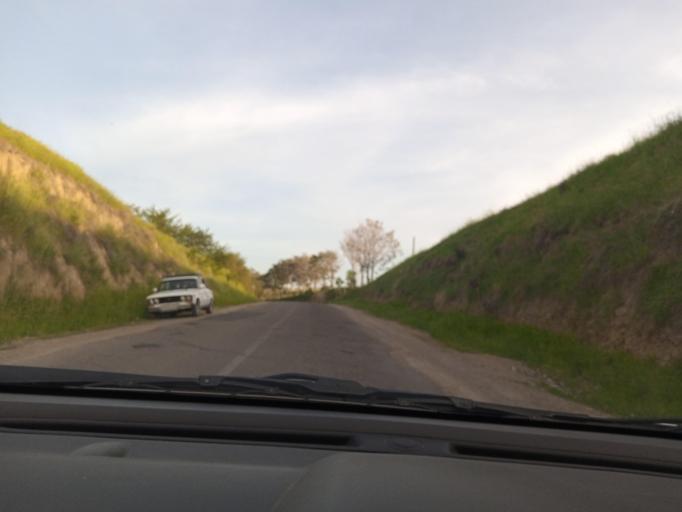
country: UZ
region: Toshkent
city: Parkent
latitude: 41.2387
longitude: 69.7336
